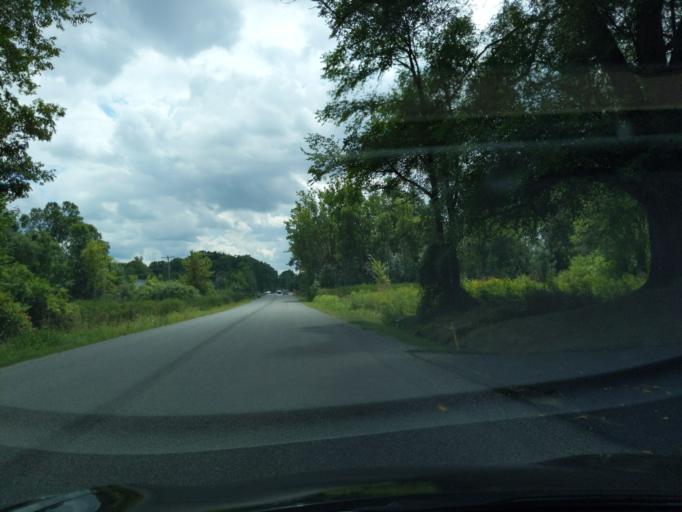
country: US
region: Michigan
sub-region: Eaton County
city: Dimondale
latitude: 42.6429
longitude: -84.5825
